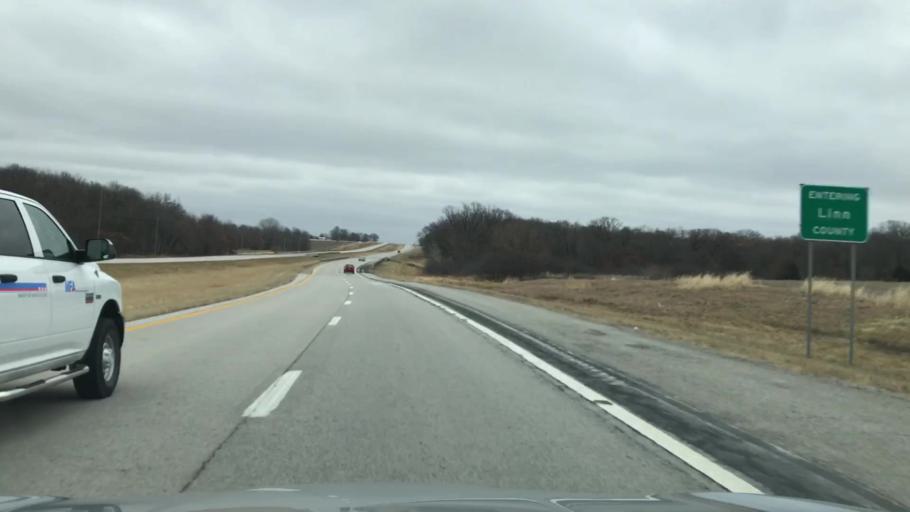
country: US
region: Missouri
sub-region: Livingston County
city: Chillicothe
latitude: 39.7772
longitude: -93.3638
